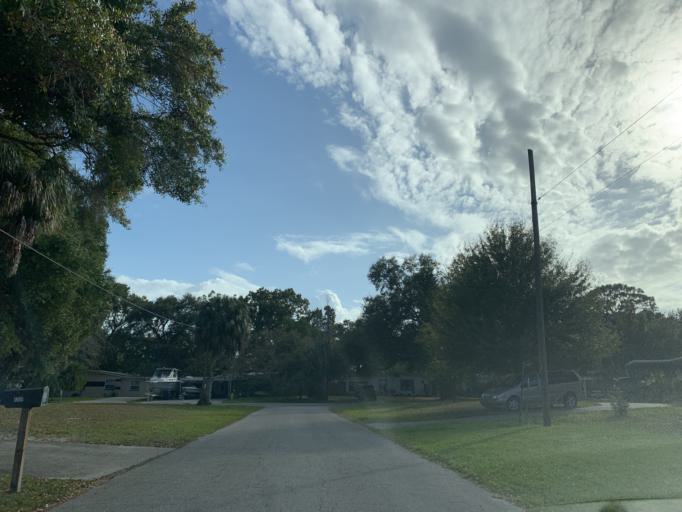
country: US
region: Florida
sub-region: Hillsborough County
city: Tampa
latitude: 27.9020
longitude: -82.5115
